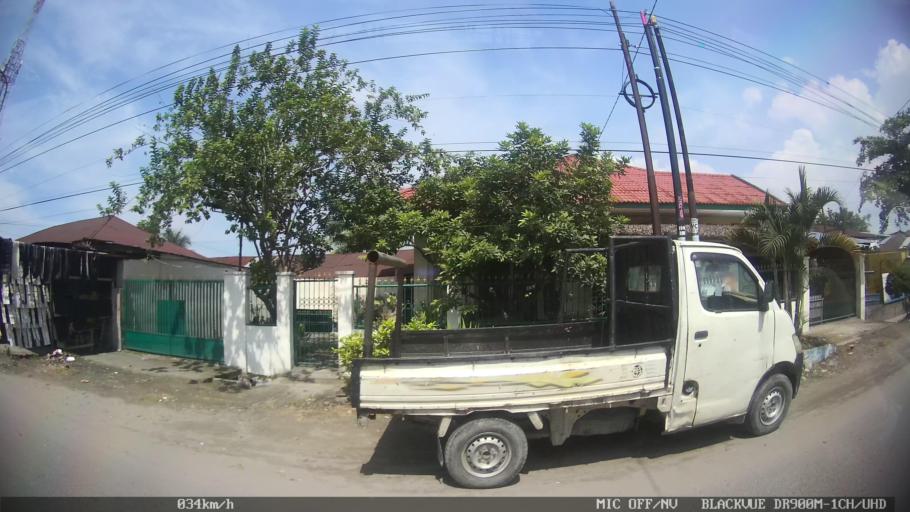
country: ID
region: North Sumatra
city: Medan
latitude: 3.6443
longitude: 98.6576
